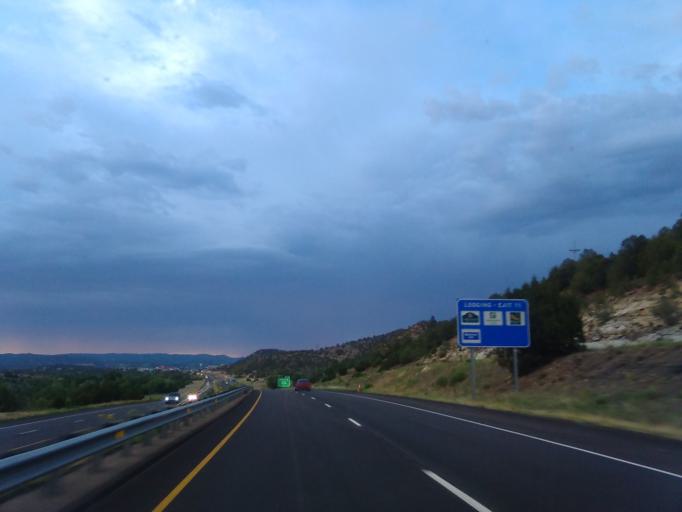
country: US
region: Colorado
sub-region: Las Animas County
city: Trinidad
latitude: 37.1140
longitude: -104.5211
